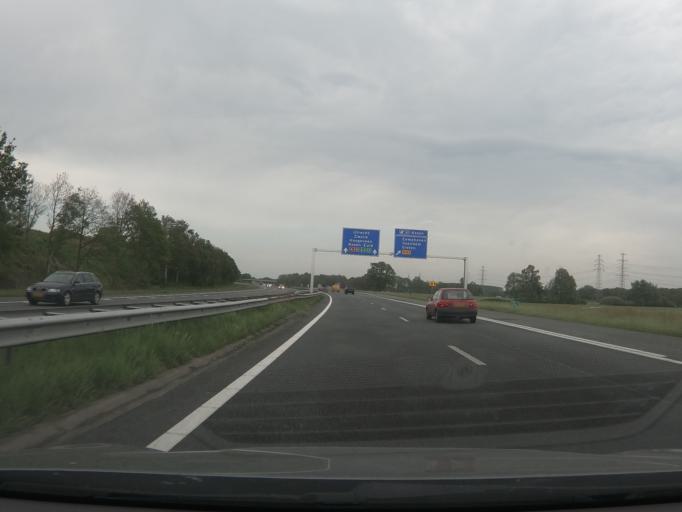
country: NL
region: Drenthe
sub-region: Gemeente Assen
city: Assen
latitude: 52.9798
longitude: 6.5293
